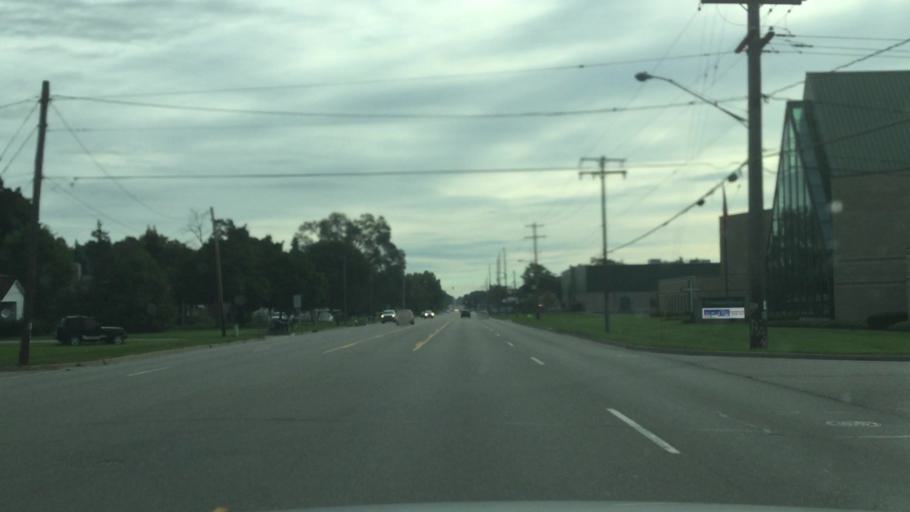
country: US
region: Michigan
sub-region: Genesee County
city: Flint
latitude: 42.9739
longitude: -83.7031
